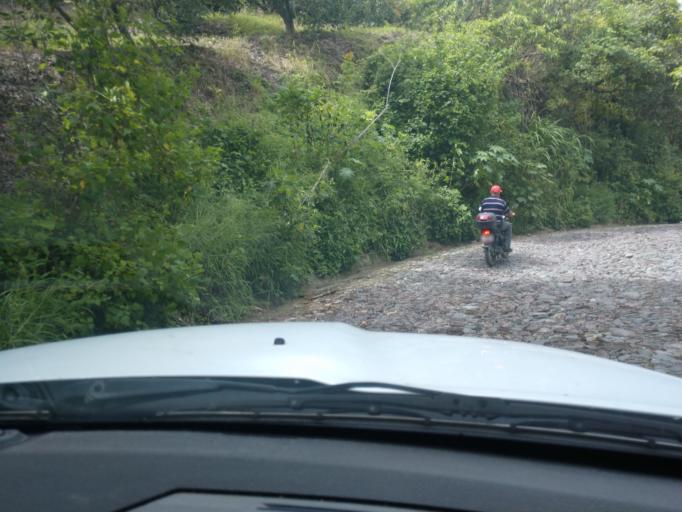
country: MX
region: Nayarit
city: Xalisco
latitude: 21.4404
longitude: -104.9148
